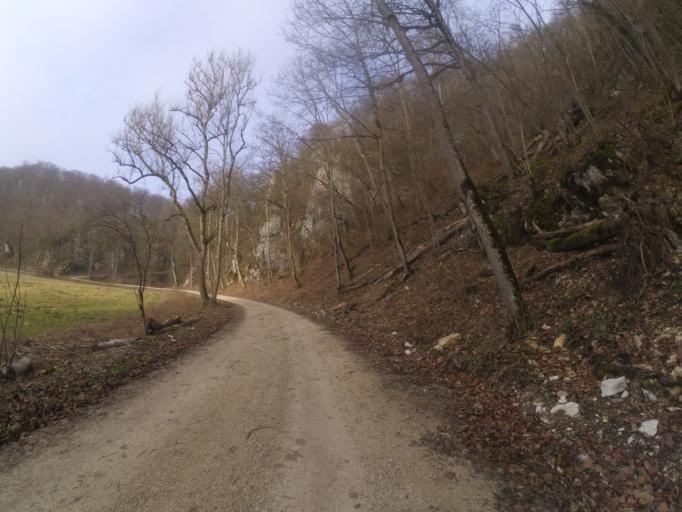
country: DE
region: Baden-Wuerttemberg
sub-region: Tuebingen Region
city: Rechtenstein
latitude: 48.2611
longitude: 9.5570
